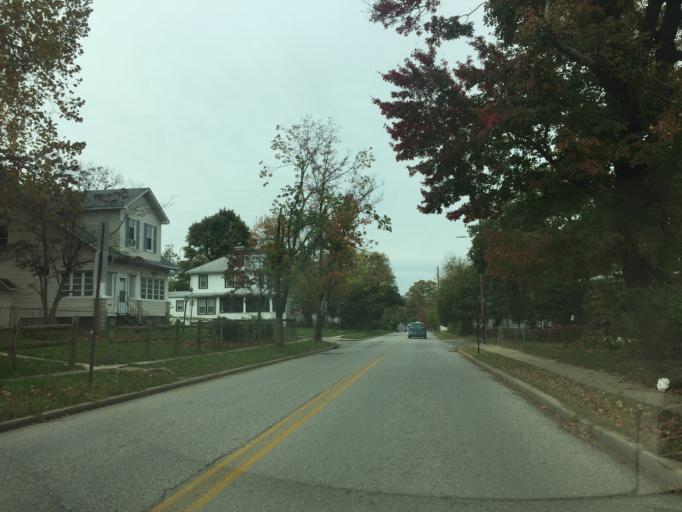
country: US
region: Maryland
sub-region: Baltimore County
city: Parkville
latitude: 39.3562
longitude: -76.5666
